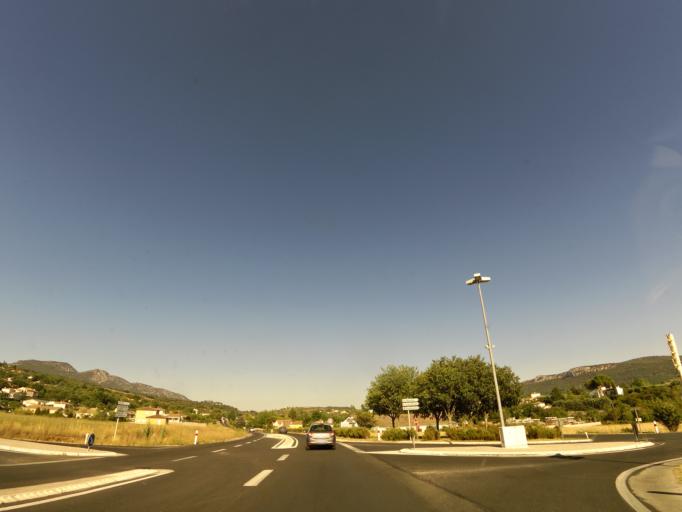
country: FR
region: Languedoc-Roussillon
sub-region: Departement de l'Herault
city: Laroque
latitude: 43.9434
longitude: 3.7264
